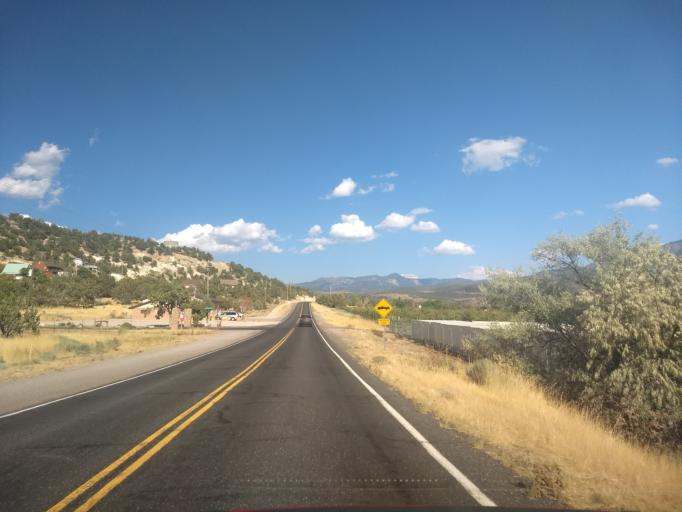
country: US
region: Utah
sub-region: Washington County
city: Enterprise
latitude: 37.4170
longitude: -113.6300
